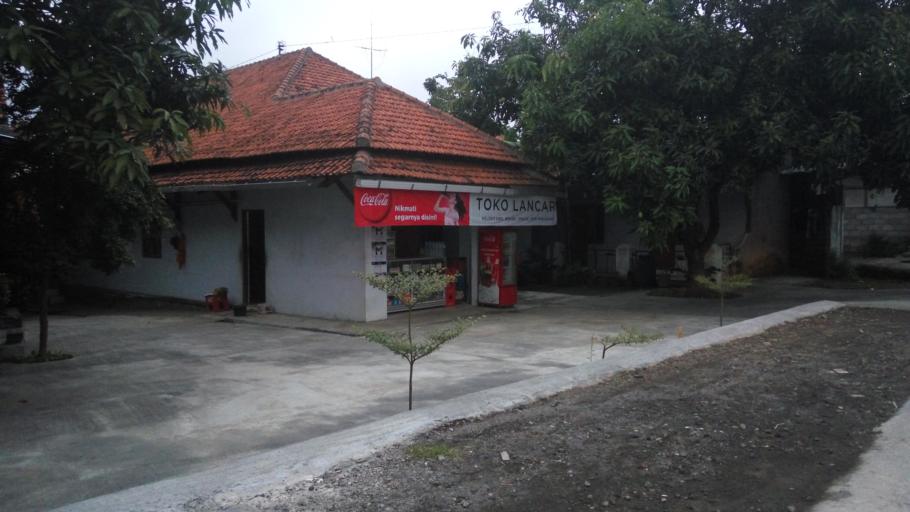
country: ID
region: Central Java
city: Ambarawa
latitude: -7.2149
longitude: 110.4261
